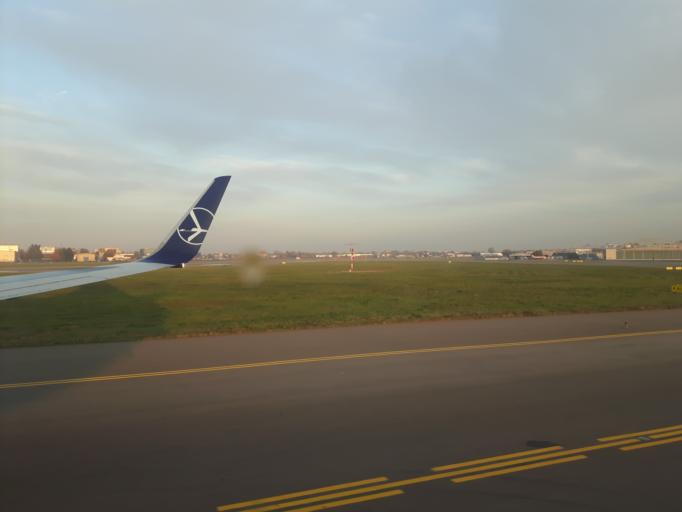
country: PL
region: Masovian Voivodeship
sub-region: Warszawa
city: Wlochy
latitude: 52.1758
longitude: 20.9610
